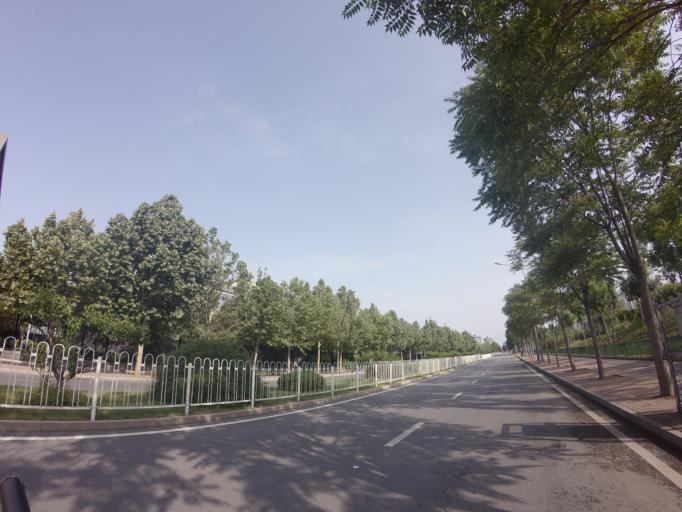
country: CN
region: Beijing
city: Xibeiwang
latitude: 40.0709
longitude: 116.2460
